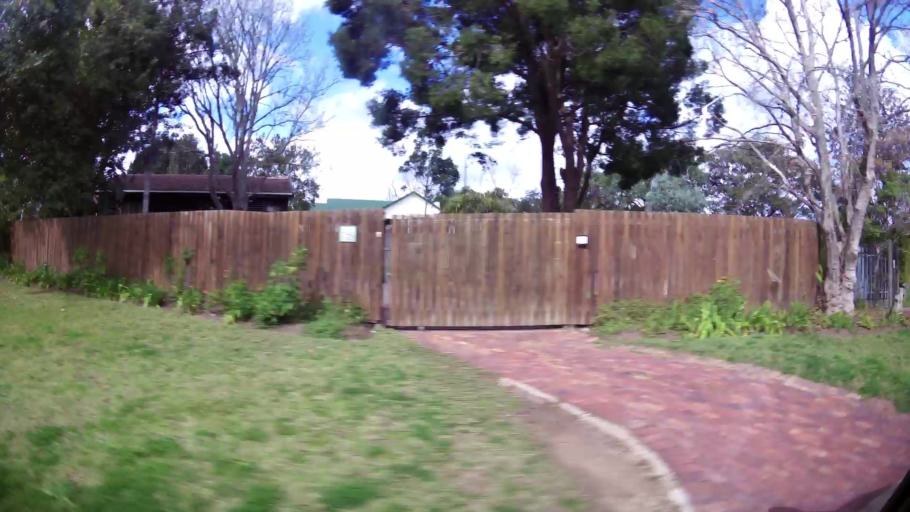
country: ZA
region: Western Cape
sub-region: Eden District Municipality
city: Knysna
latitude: -34.0613
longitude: 23.0801
